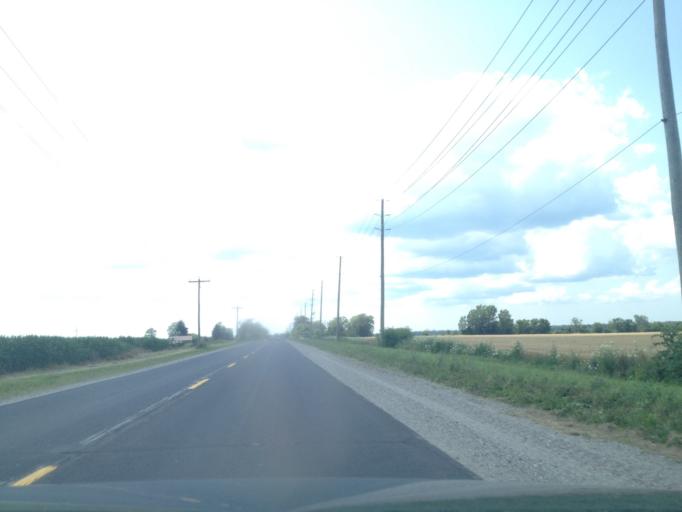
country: CA
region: Ontario
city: Aylmer
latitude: 42.6683
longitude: -80.8374
